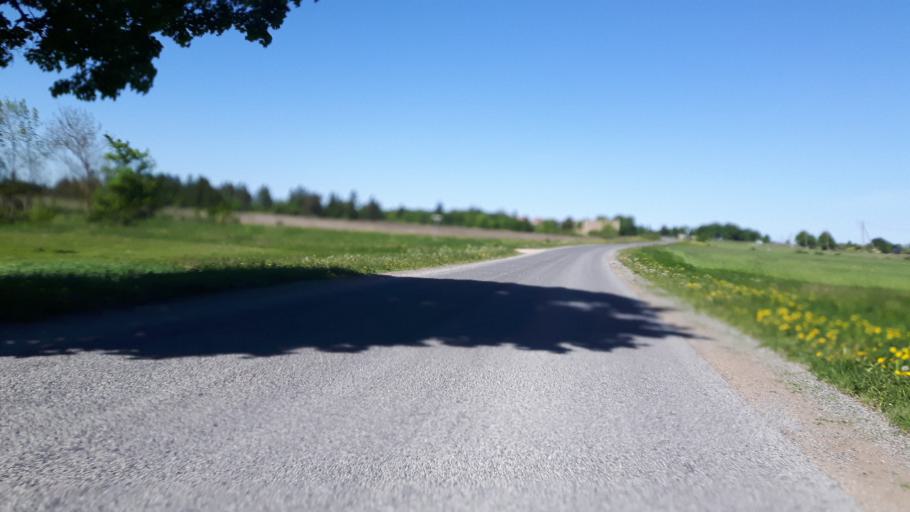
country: EE
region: Ida-Virumaa
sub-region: Sillamaee linn
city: Sillamae
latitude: 59.3838
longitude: 27.8132
